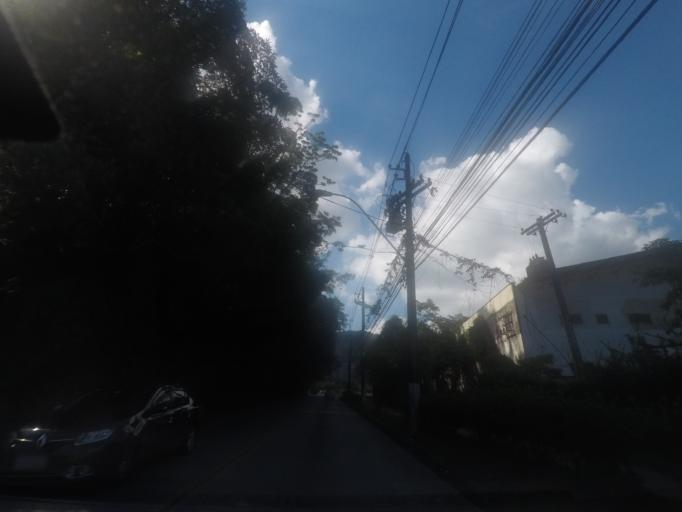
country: BR
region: Rio de Janeiro
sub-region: Petropolis
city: Petropolis
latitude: -22.5312
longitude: -43.2118
